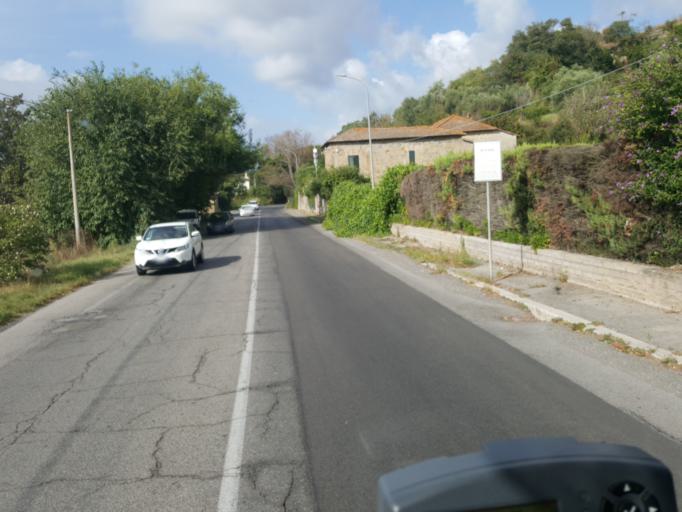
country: IT
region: Latium
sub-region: Citta metropolitana di Roma Capitale
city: Girardi-Bellavista-Terrazze
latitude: 42.0961
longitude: 12.5736
